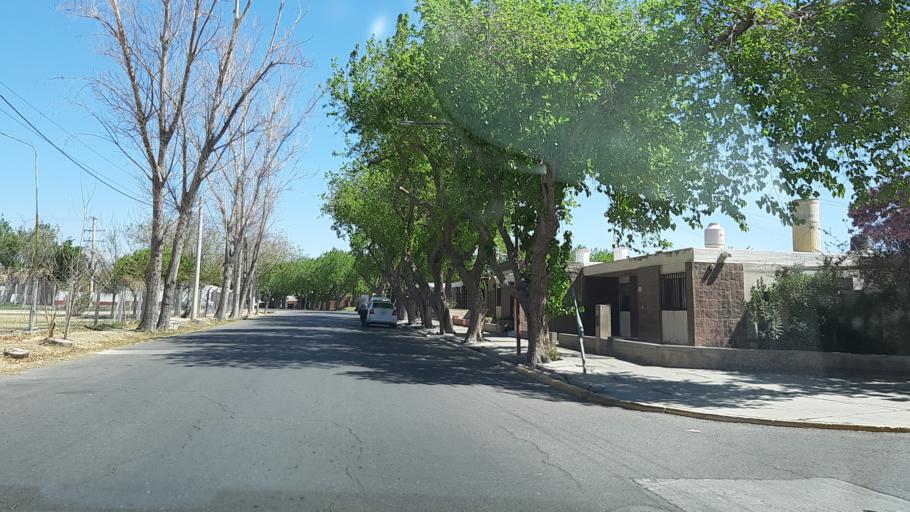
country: AR
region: San Juan
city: San Juan
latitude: -31.5263
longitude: -68.5440
